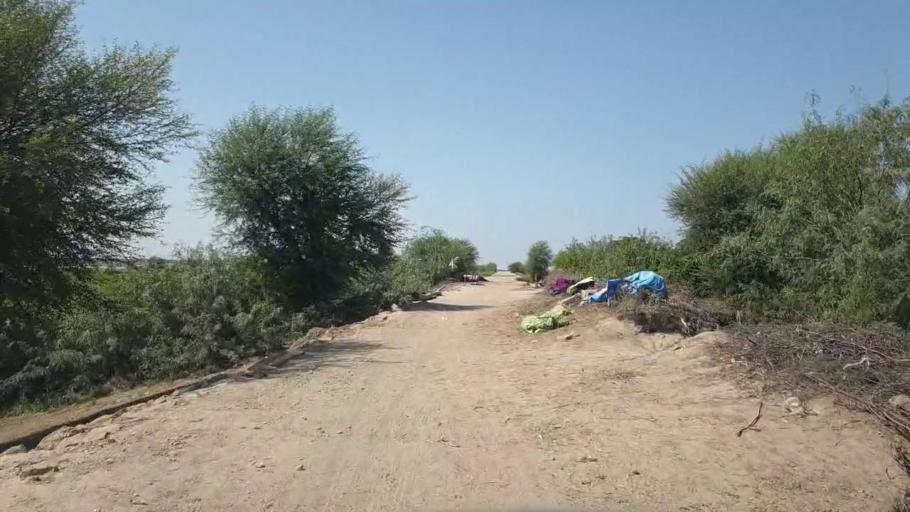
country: PK
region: Sindh
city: Matiari
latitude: 25.6339
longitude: 68.4888
